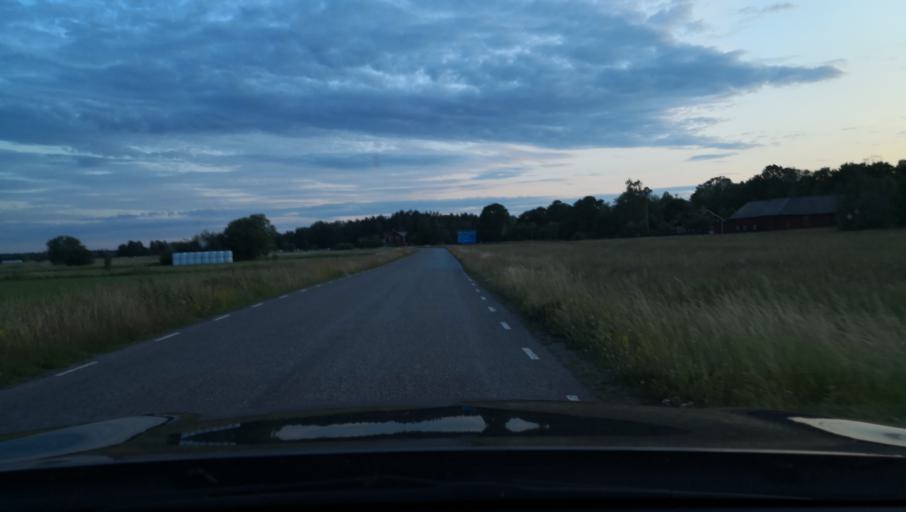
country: SE
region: Uppsala
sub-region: Osthammars Kommun
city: Bjorklinge
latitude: 60.0471
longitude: 17.5025
